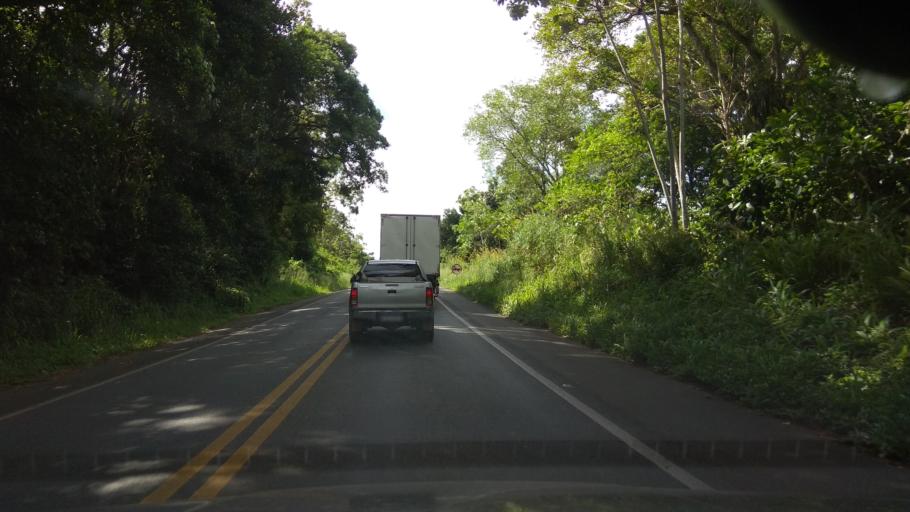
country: BR
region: Bahia
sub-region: Urucuca
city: Urucuca
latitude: -14.6280
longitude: -39.3329
